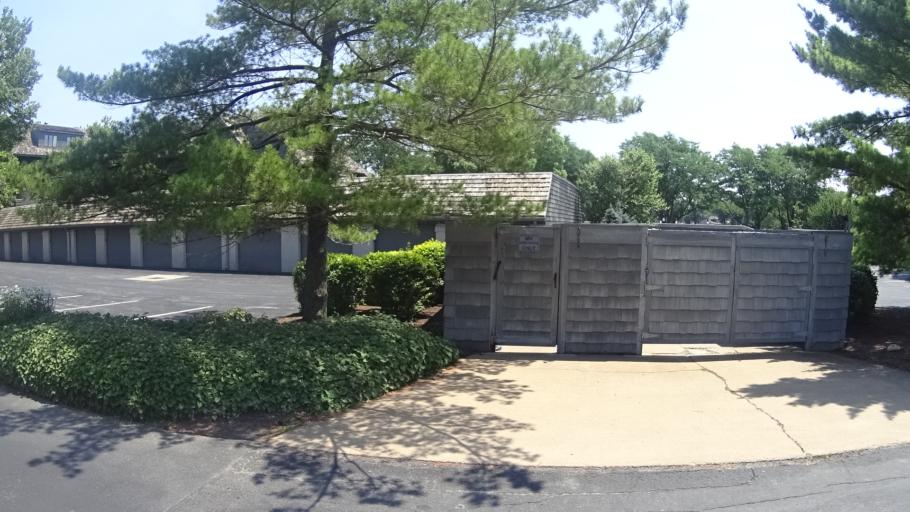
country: US
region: Ohio
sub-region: Erie County
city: Huron
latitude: 41.4134
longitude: -82.5943
